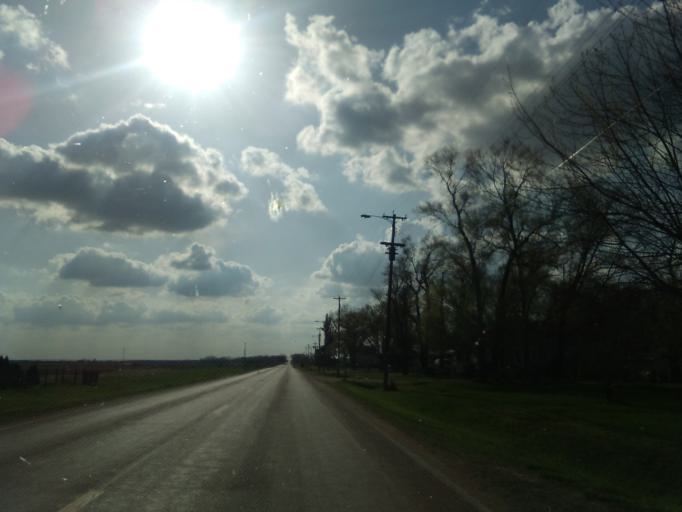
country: US
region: Nebraska
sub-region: Webster County
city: Red Cloud
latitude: 40.0888
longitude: -98.5328
